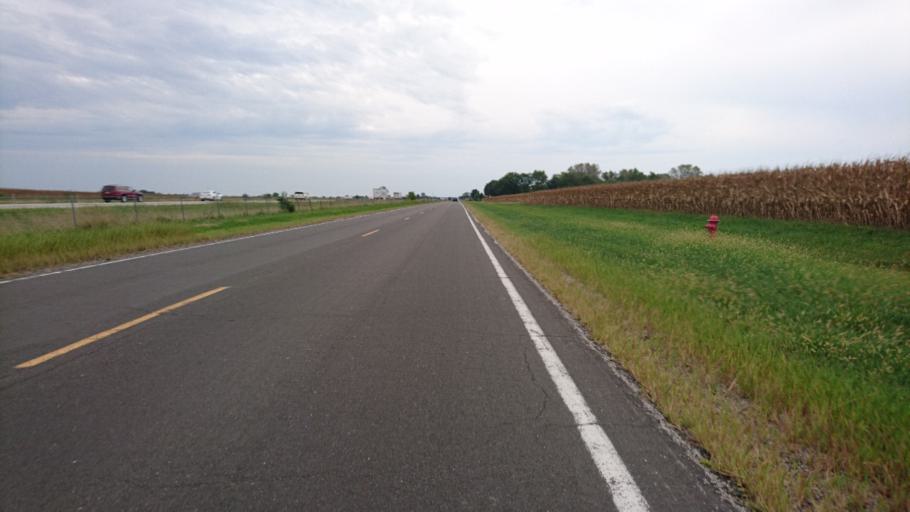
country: US
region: Illinois
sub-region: Sangamon County
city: Chatham
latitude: 39.6621
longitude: -89.6480
